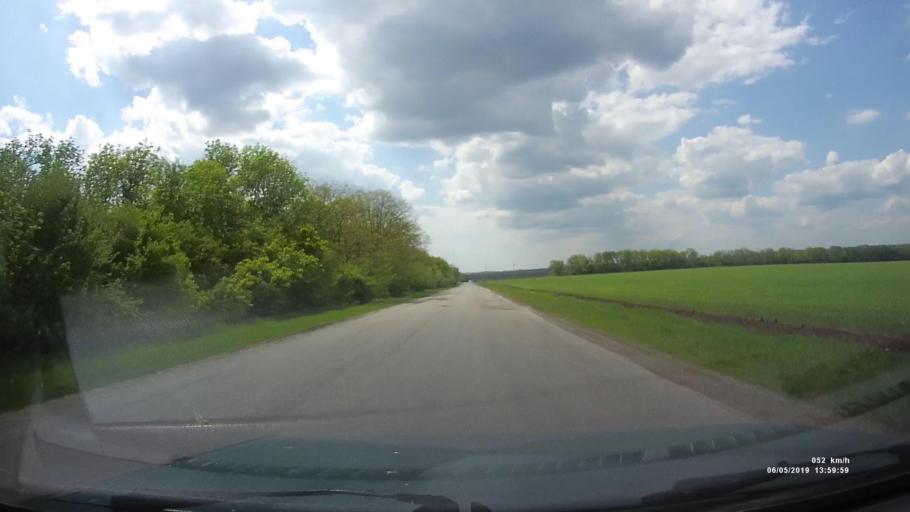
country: RU
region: Rostov
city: Shakhty
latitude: 47.6854
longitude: 40.3947
